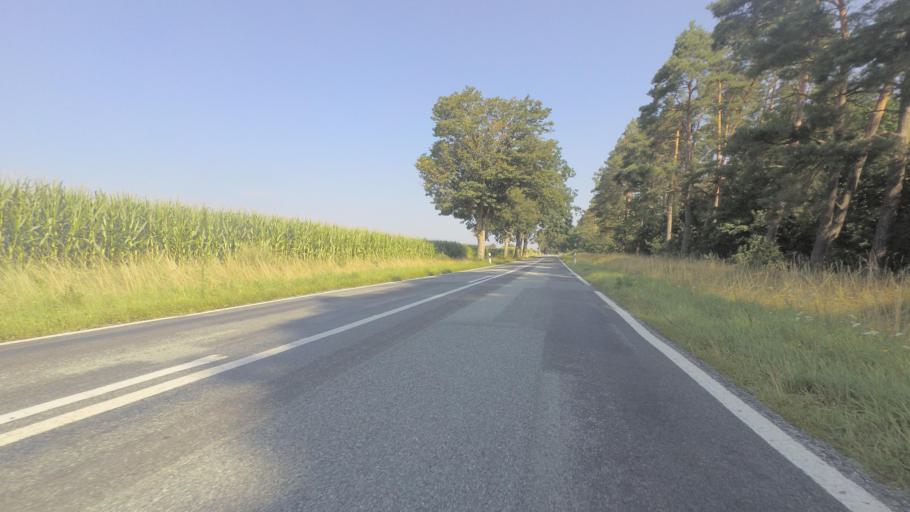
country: DE
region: Mecklenburg-Vorpommern
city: Grabowhofe
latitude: 53.6032
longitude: 12.4692
